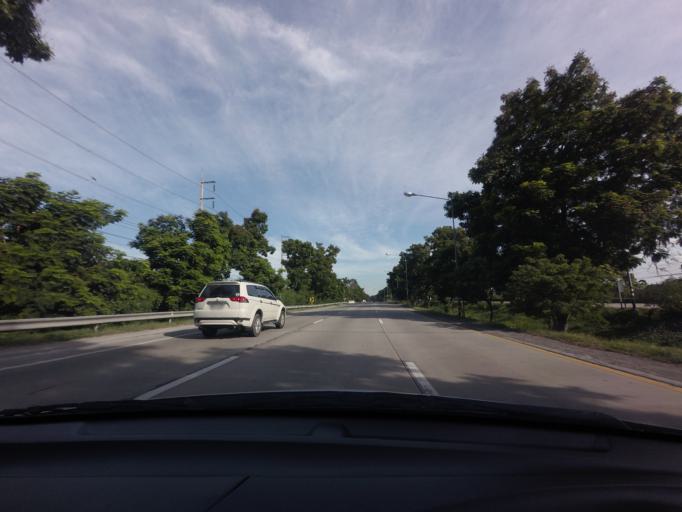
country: TH
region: Suphan Buri
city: Bang Pla Ma
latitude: 14.4218
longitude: 100.1499
